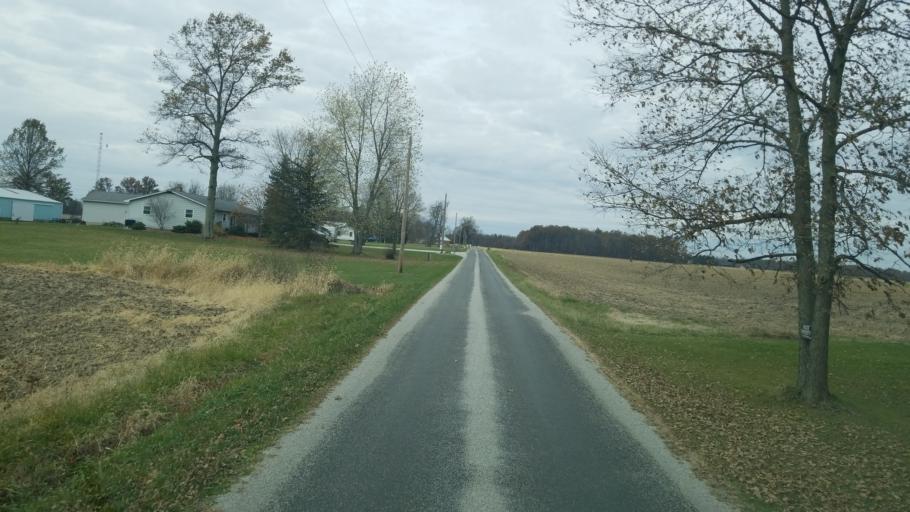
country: US
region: Ohio
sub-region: Morrow County
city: Cardington
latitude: 40.5504
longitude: -82.9816
